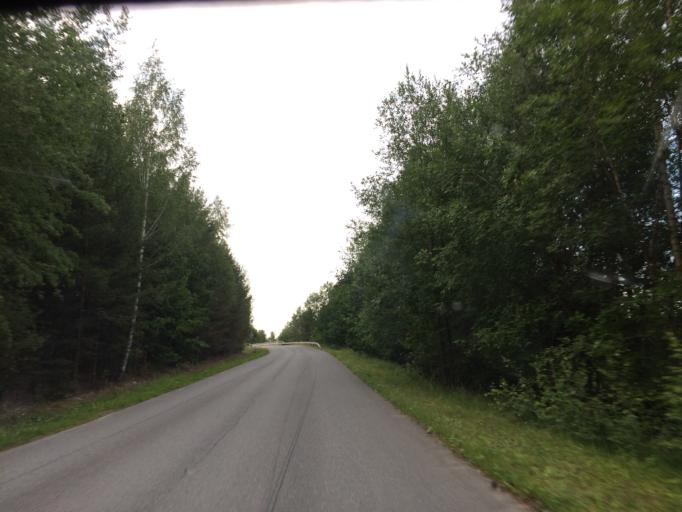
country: FI
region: Haeme
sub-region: Haemeenlinna
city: Tervakoski
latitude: 60.8423
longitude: 24.6266
